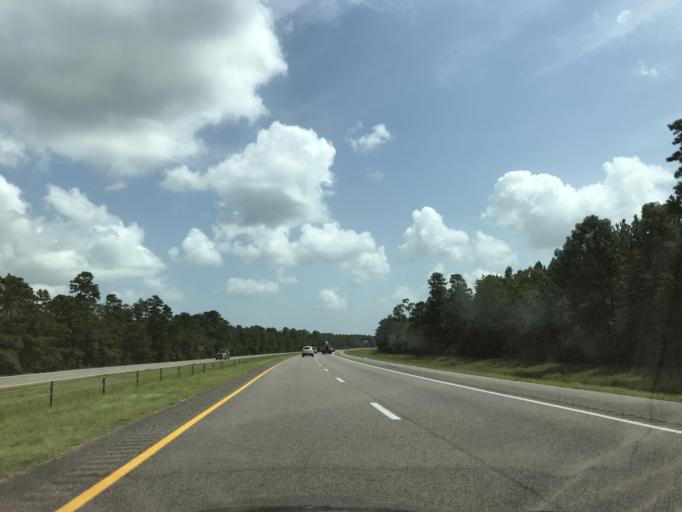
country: US
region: North Carolina
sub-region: Pender County
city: Burgaw
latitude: 34.5146
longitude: -77.8820
